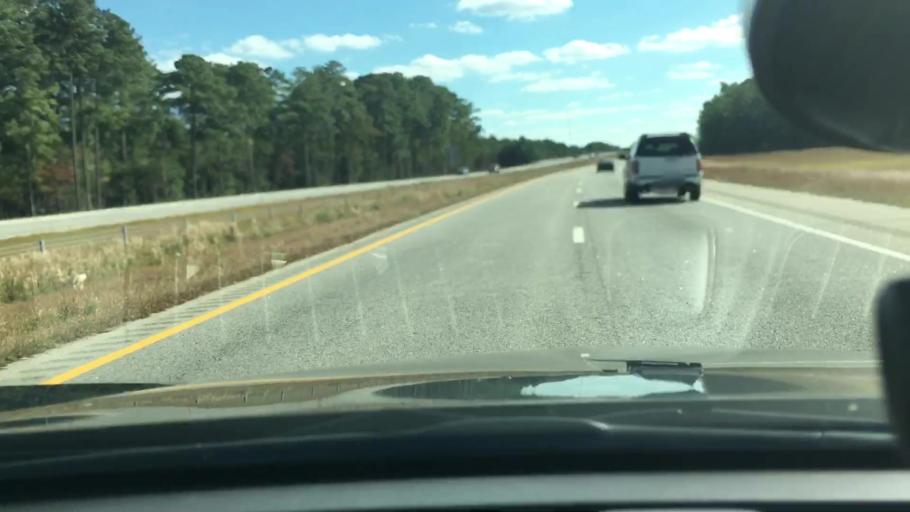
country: US
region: North Carolina
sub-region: Wilson County
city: Lucama
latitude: 35.7596
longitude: -78.0270
